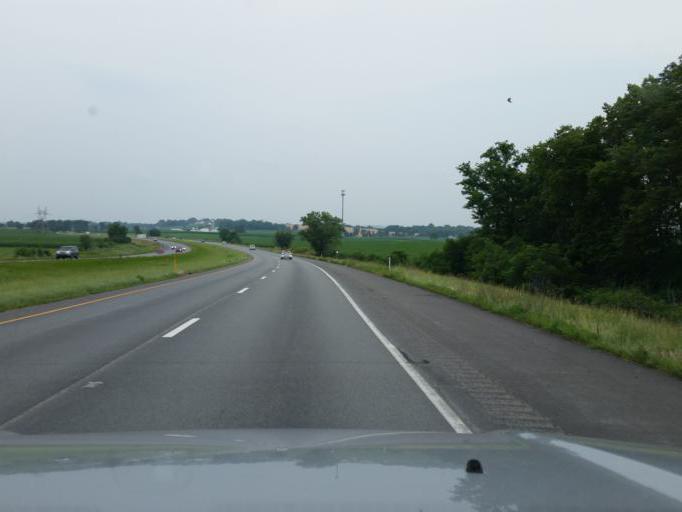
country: US
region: Pennsylvania
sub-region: Lancaster County
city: Rheems
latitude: 40.1355
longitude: -76.5453
